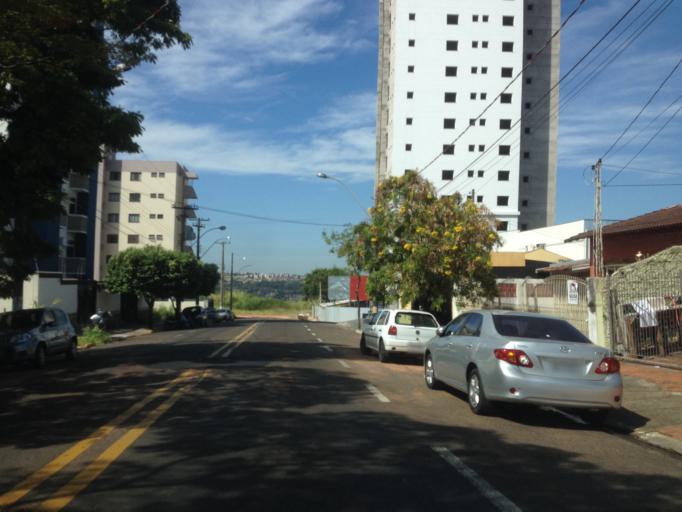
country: BR
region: Sao Paulo
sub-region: Marilia
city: Marilia
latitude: -22.2263
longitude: -49.9502
